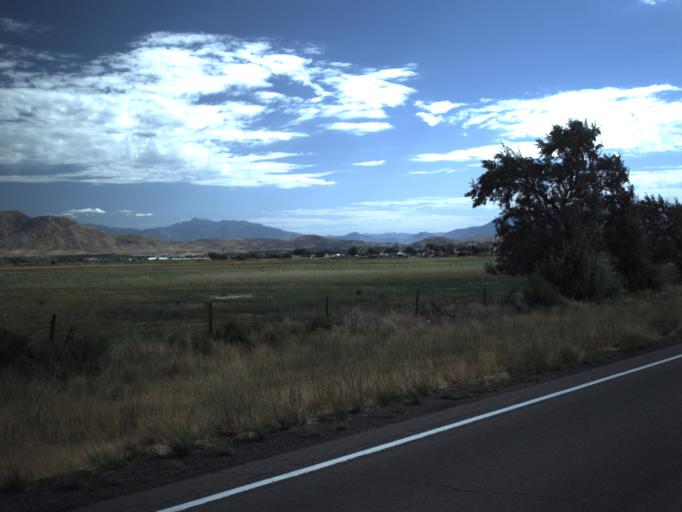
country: US
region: Utah
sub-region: Utah County
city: Genola
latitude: 39.9525
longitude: -111.9142
